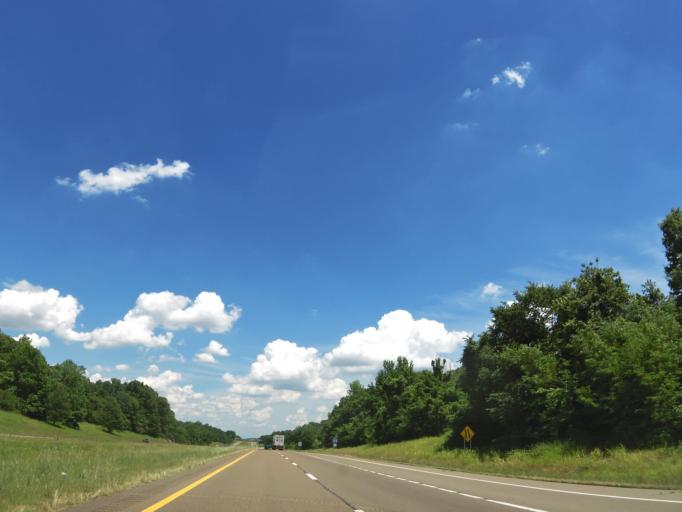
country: US
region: Tennessee
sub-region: Dyer County
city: Dyersburg
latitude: 36.0739
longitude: -89.4838
